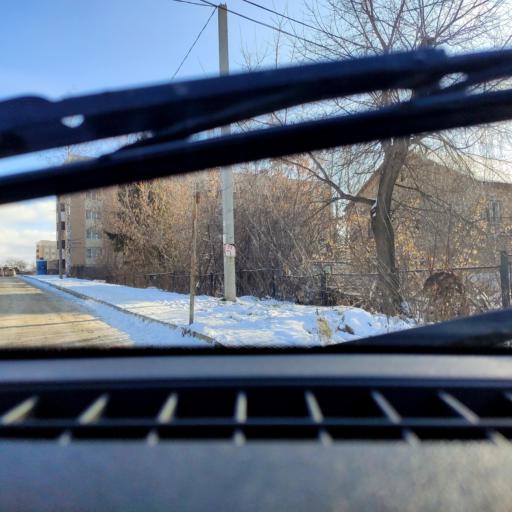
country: RU
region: Bashkortostan
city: Iglino
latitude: 54.8182
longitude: 56.3948
